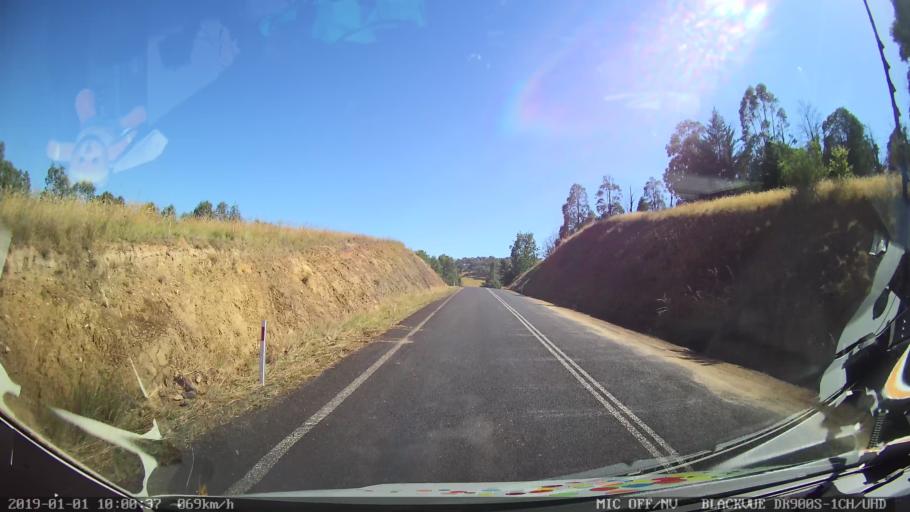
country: AU
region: New South Wales
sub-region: Snowy River
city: Jindabyne
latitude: -36.2001
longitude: 148.1022
